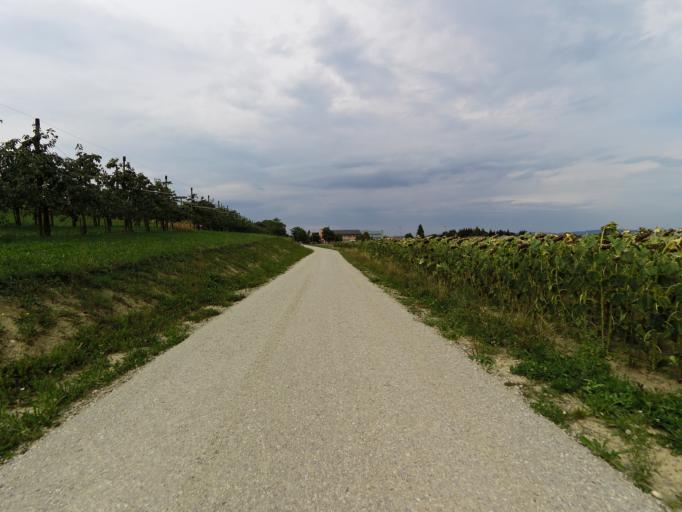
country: CH
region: Thurgau
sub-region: Kreuzlingen District
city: Ermatingen
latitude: 47.6645
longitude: 9.0623
